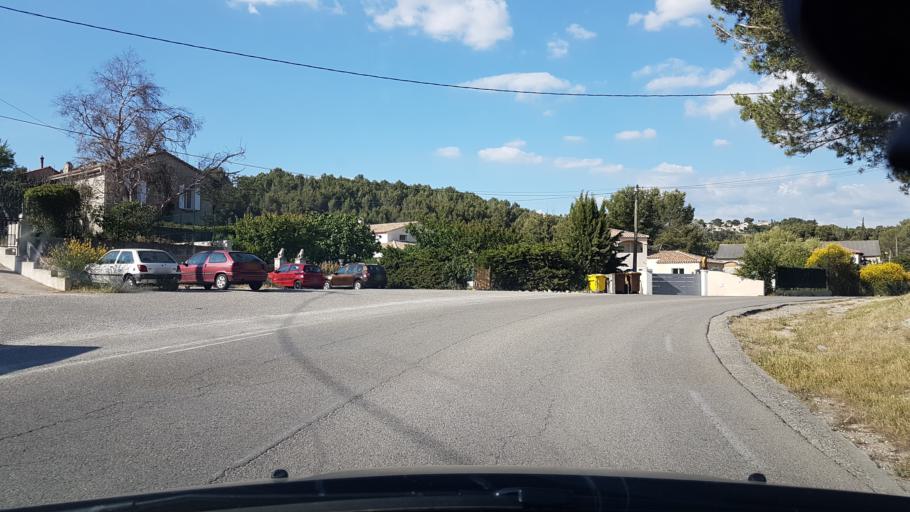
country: FR
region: Provence-Alpes-Cote d'Azur
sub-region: Departement des Bouches-du-Rhone
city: Carnoux-en-Provence
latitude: 43.2441
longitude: 5.5662
